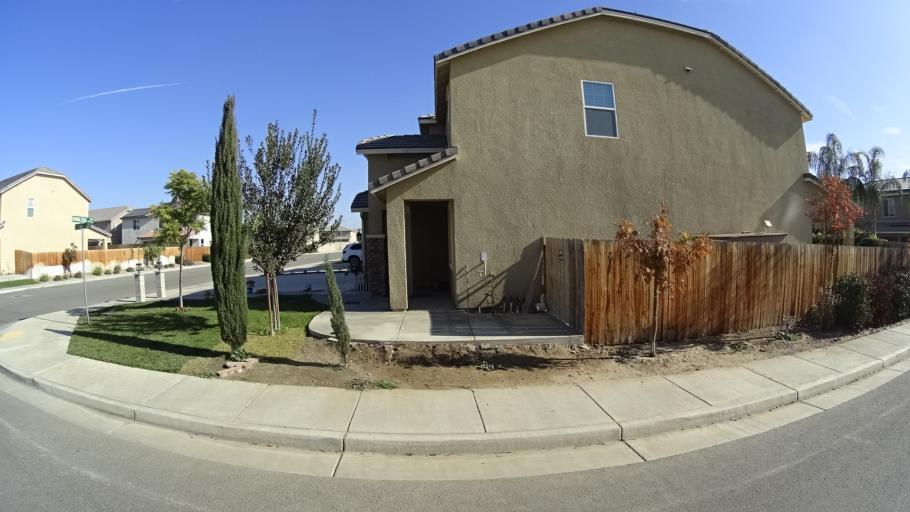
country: US
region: California
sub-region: Kern County
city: Greenfield
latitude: 35.2873
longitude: -119.0603
